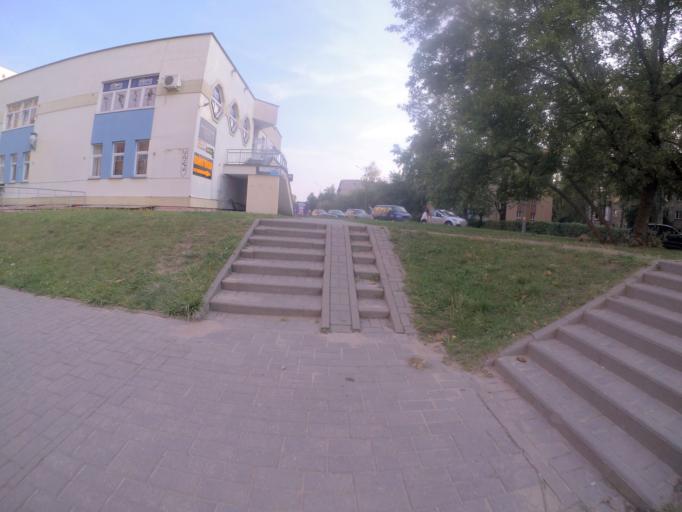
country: BY
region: Grodnenskaya
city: Hrodna
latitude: 53.6958
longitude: 23.8353
